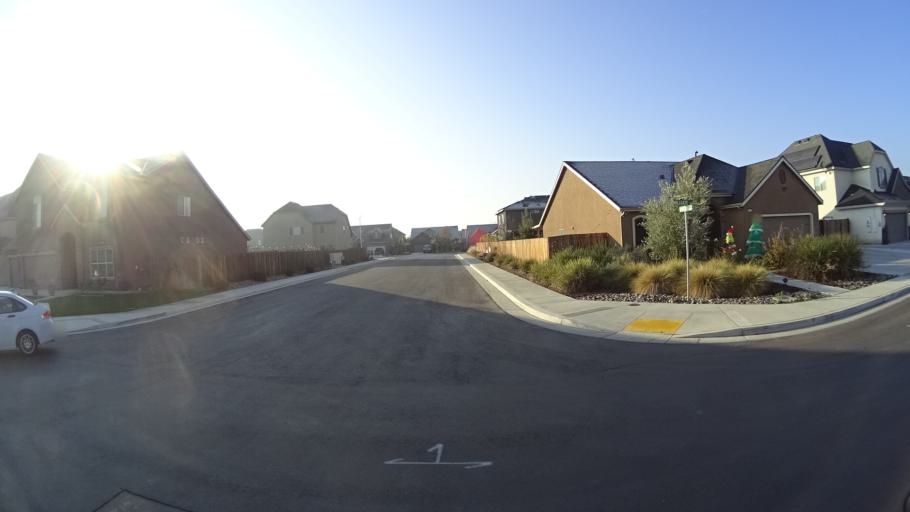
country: US
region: California
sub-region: Kern County
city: Greenacres
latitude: 35.2921
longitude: -119.1170
